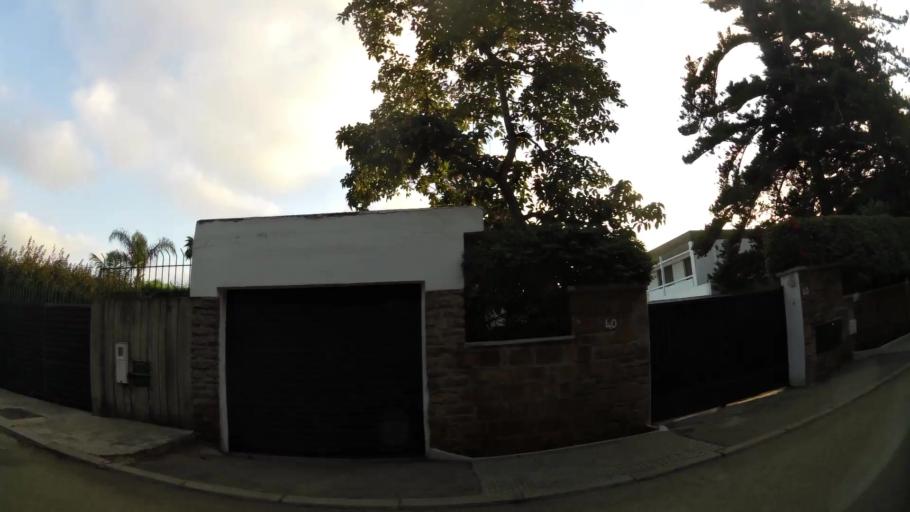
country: MA
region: Rabat-Sale-Zemmour-Zaer
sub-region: Rabat
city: Rabat
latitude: 33.9777
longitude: -6.8325
